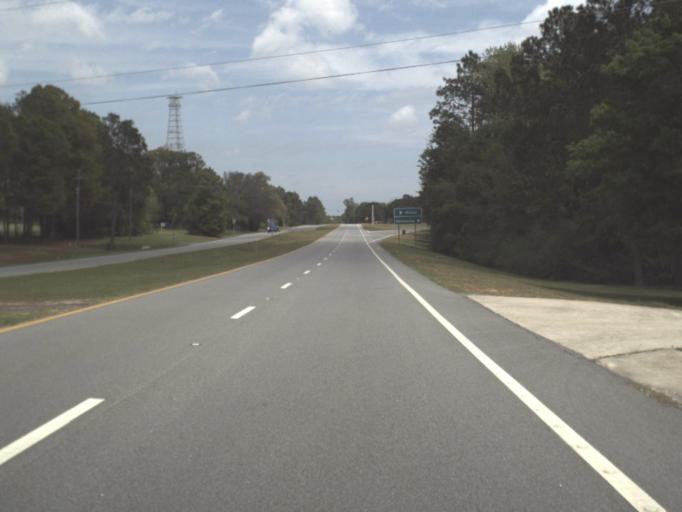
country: US
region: Florida
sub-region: Escambia County
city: Cantonment
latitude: 30.5346
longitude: -87.4131
